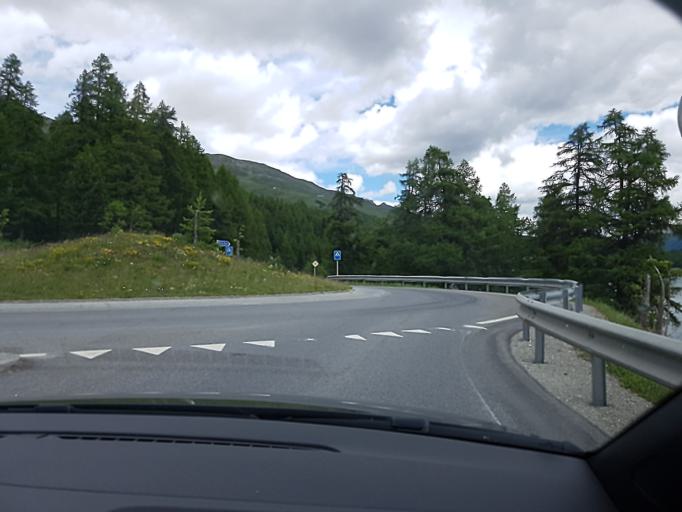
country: CH
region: Grisons
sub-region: Maloja District
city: Silvaplana
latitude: 46.4680
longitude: 9.8020
